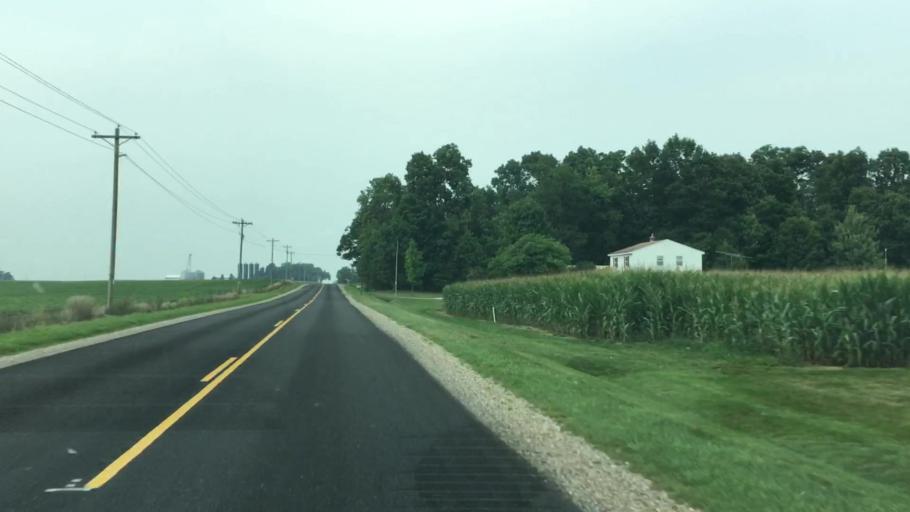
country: US
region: Michigan
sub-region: Ottawa County
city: Hudsonville
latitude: 42.7872
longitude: -85.9010
